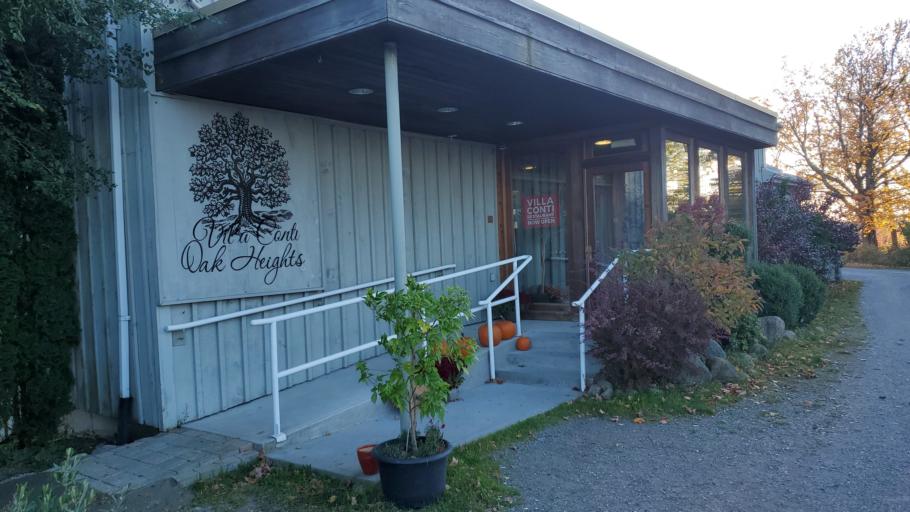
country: CA
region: Ontario
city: Cobourg
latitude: 44.1448
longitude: -77.9824
